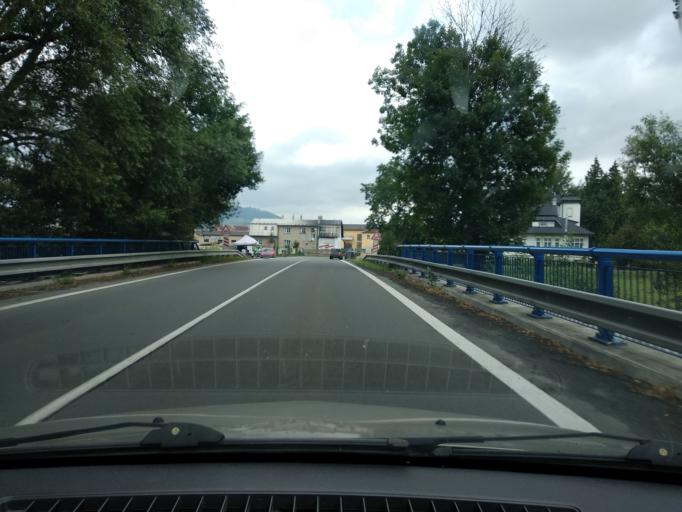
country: CZ
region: Olomoucky
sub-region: Okres Sumperk
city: Bludov
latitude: 49.9268
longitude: 16.9197
